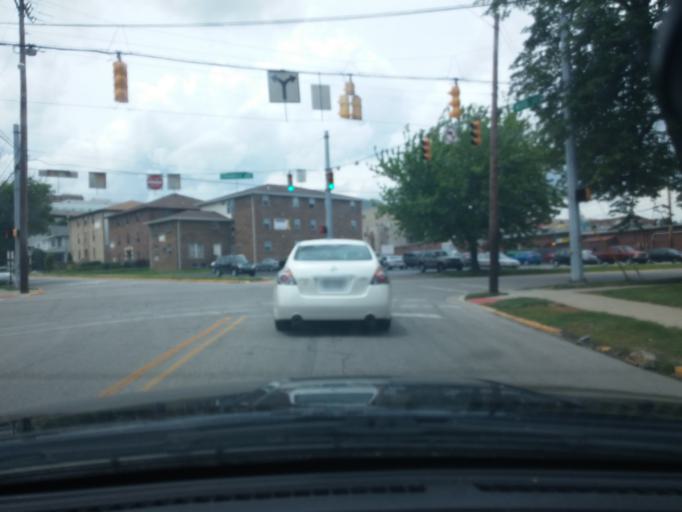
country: US
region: Indiana
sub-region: Tippecanoe County
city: West Lafayette
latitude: 40.4219
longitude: -86.9072
